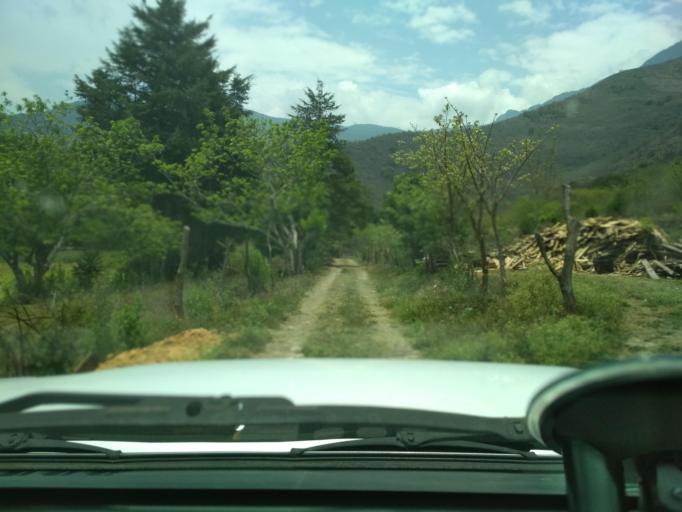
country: MX
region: Veracruz
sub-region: Nogales
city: Taza de Agua Ojo Zarco
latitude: 18.7750
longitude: -97.2071
